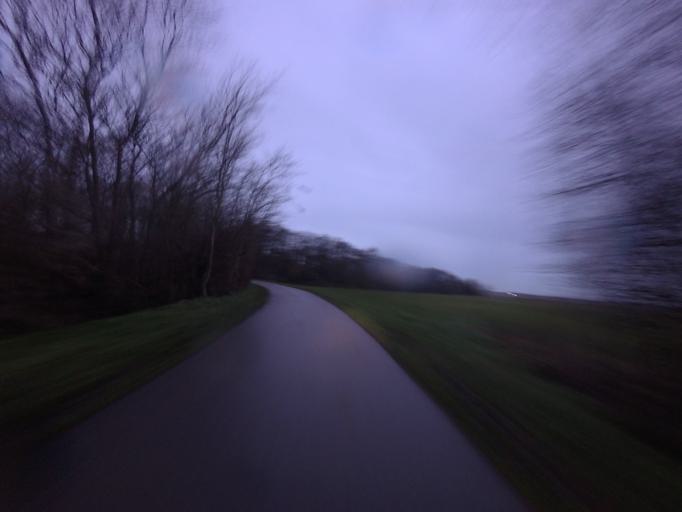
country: NL
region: North Holland
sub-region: Gemeente Texel
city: Den Burg
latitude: 53.0679
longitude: 4.7951
